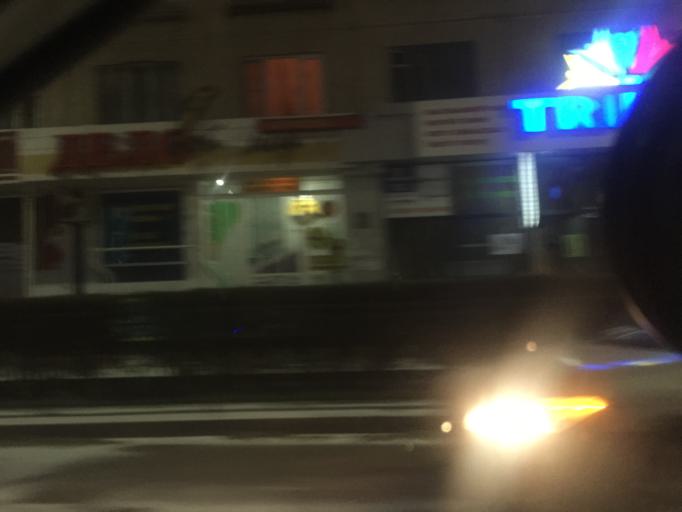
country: KZ
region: Astana Qalasy
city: Astana
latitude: 51.1814
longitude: 71.4172
